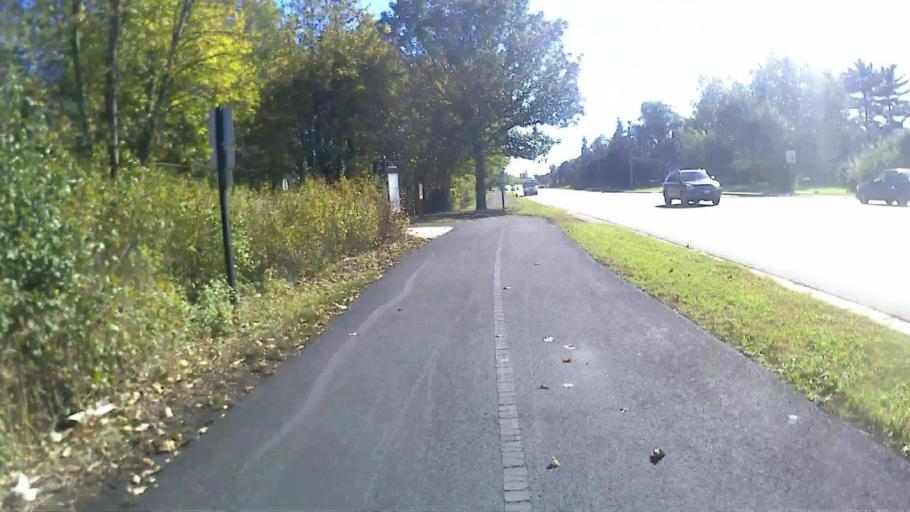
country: US
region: Illinois
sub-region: DuPage County
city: Wood Dale
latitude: 41.9546
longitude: -87.9890
